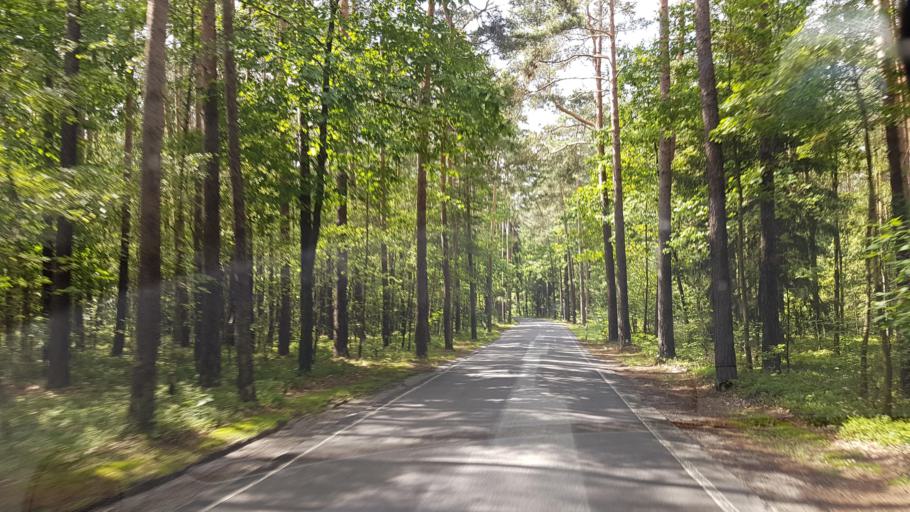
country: DE
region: Saxony
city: Hockendorf
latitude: 51.2376
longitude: 13.9092
